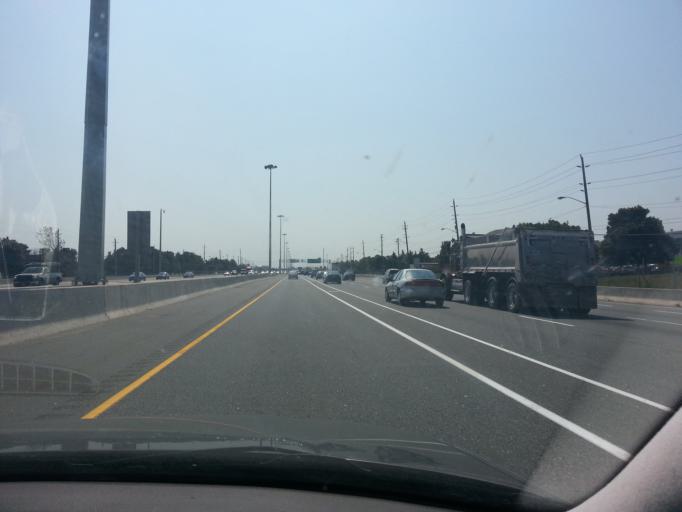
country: CA
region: Ontario
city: Burlington
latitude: 43.3895
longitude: -79.7629
